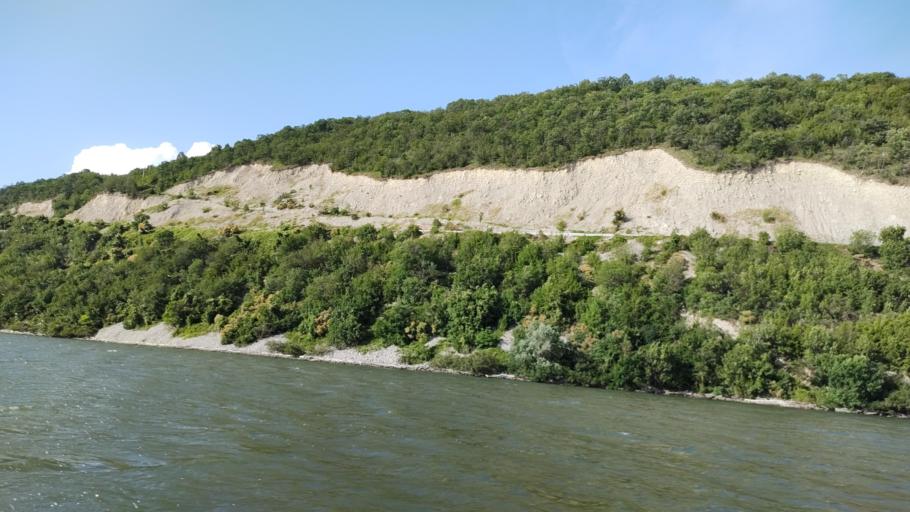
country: RO
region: Mehedinti
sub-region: Comuna Svinita
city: Svinita
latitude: 44.5038
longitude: 22.0839
